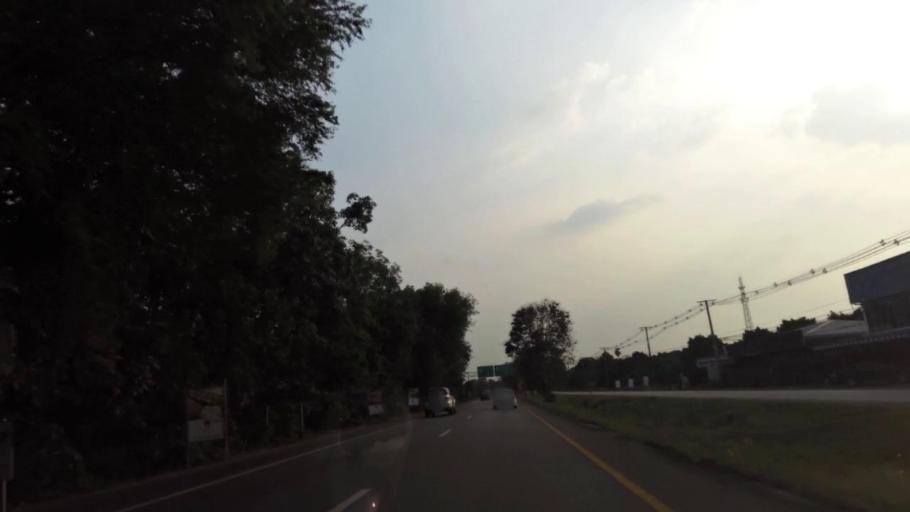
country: TH
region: Chanthaburi
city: Chanthaburi
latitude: 12.5335
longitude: 102.1575
